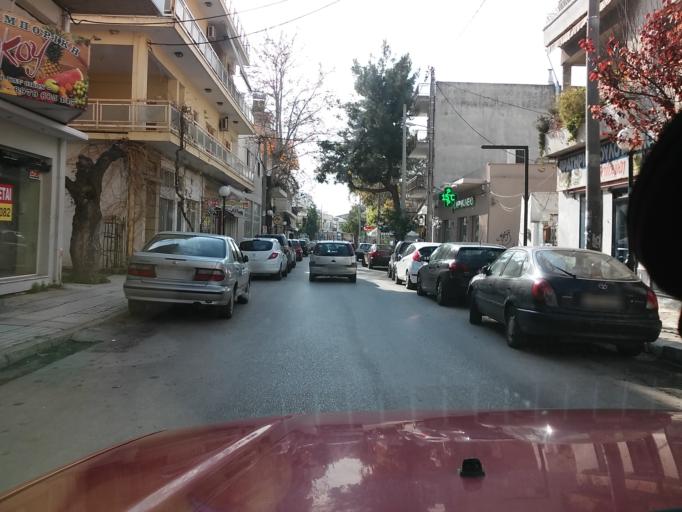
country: GR
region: Attica
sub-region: Nomarchia Athinas
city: Metamorfosi
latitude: 38.0639
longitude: 23.7614
